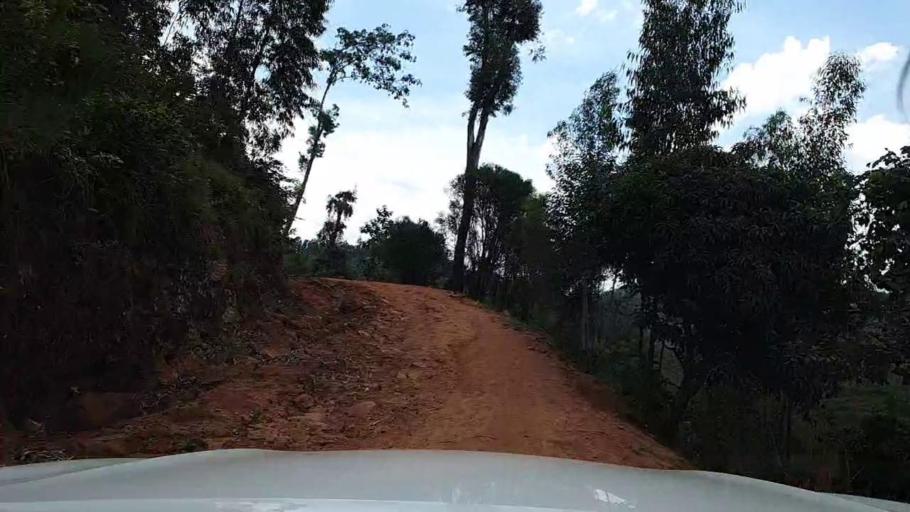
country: RW
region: Southern Province
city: Butare
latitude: -2.7475
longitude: 29.7626
